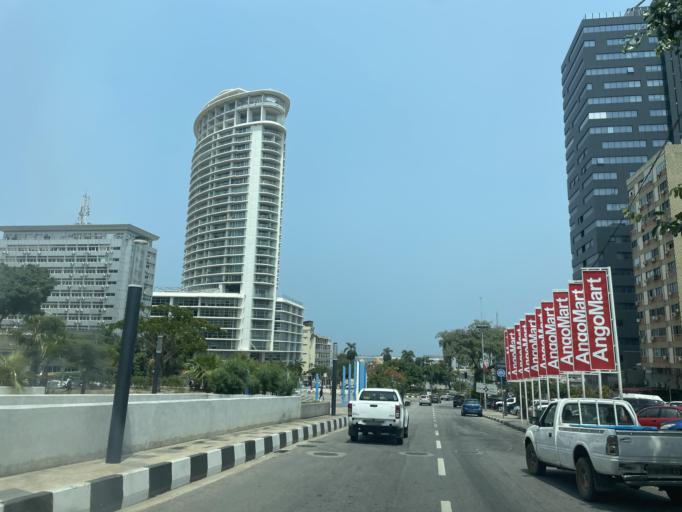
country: AO
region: Luanda
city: Luanda
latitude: -8.8094
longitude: 13.2406
